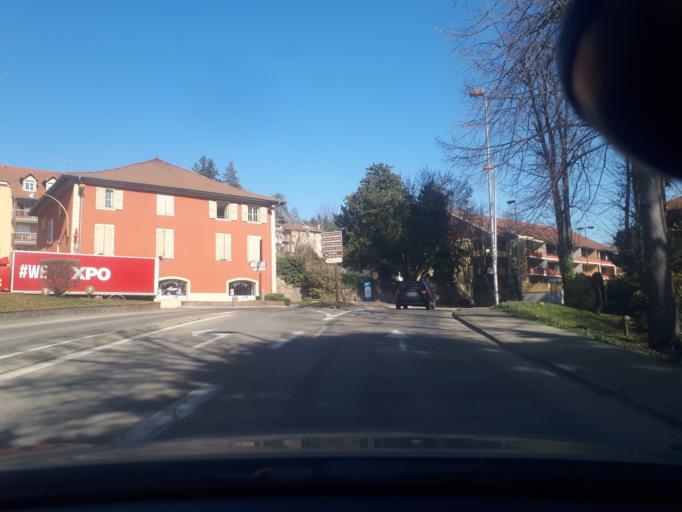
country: FR
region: Rhone-Alpes
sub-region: Departement de l'Isere
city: La Cote-Saint-Andre
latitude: 45.3930
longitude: 5.2634
